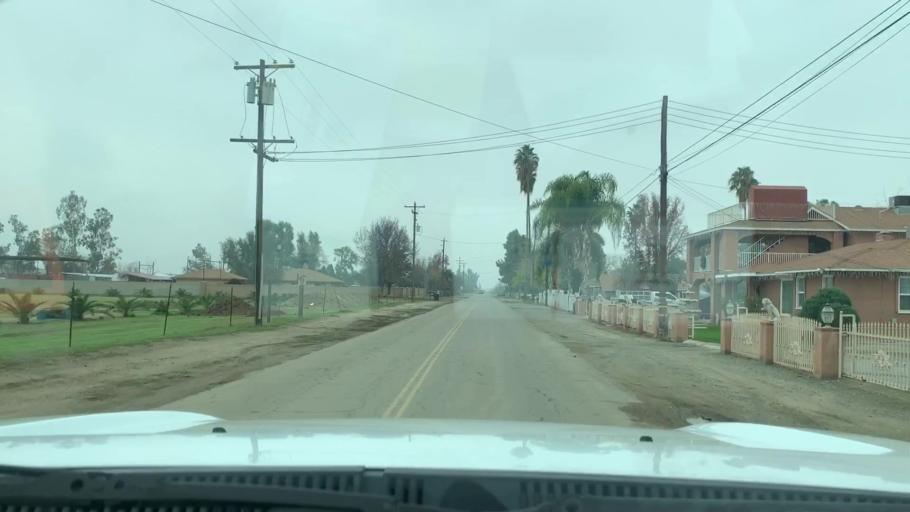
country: US
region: California
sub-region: Kern County
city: Shafter
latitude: 35.4808
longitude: -119.2964
